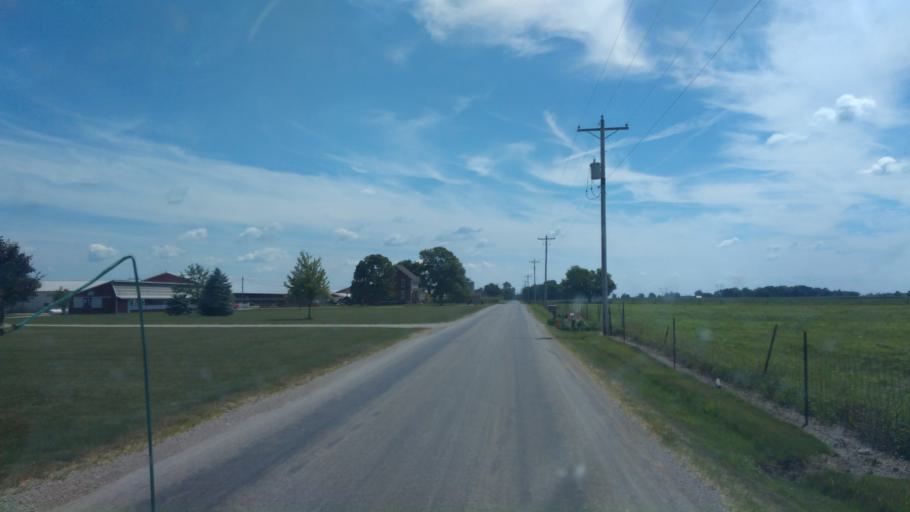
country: US
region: Indiana
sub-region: Adams County
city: Berne
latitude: 40.7011
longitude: -84.9746
